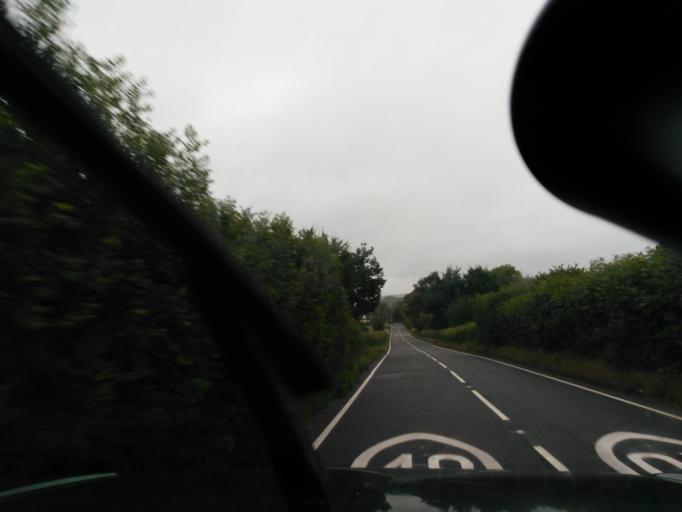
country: GB
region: England
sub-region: Dorset
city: Shaftesbury
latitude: 50.9467
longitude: -2.1934
